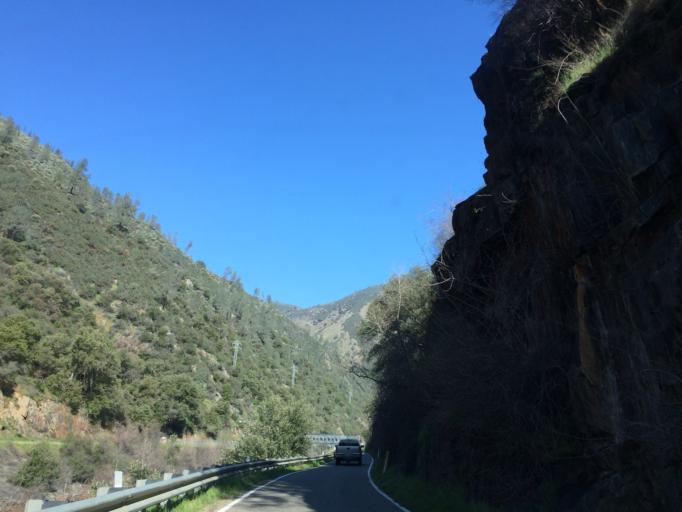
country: US
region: California
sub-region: Mariposa County
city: Midpines
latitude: 37.6582
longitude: -119.8999
